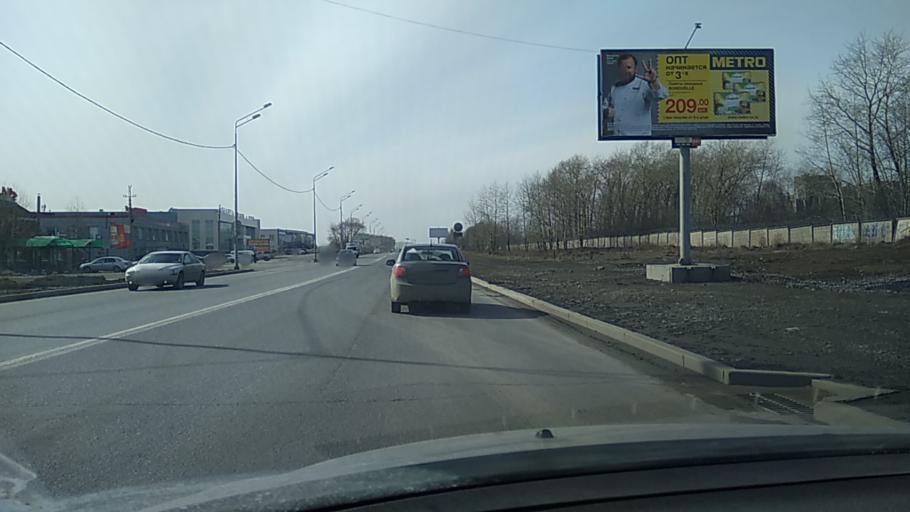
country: RU
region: Sverdlovsk
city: Nizhniy Tagil
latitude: 57.9091
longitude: 60.0282
